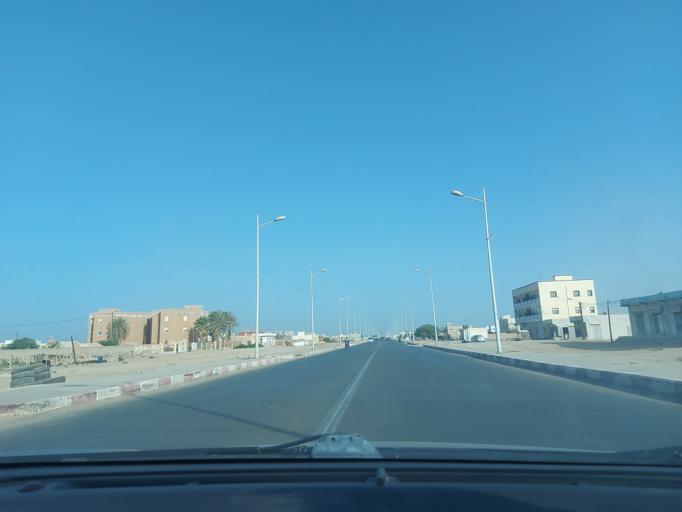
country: MR
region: Nouakchott
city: Nouakchott
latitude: 18.0893
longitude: -16.0070
